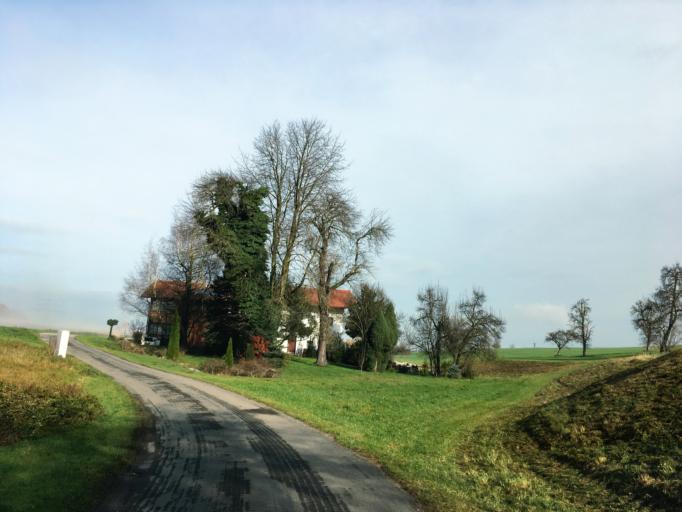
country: DE
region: Bavaria
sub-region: Upper Bavaria
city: Rosenheim
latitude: 47.8913
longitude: 12.1486
